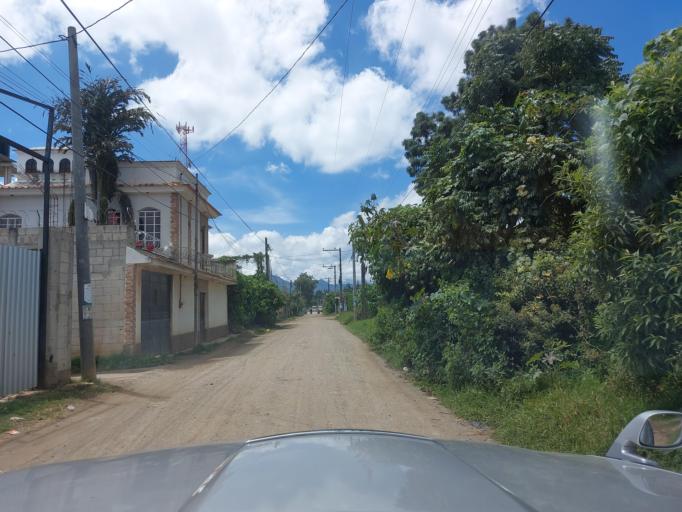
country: GT
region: Chimaltenango
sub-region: Municipio de Chimaltenango
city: Chimaltenango
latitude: 14.6485
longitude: -90.8163
